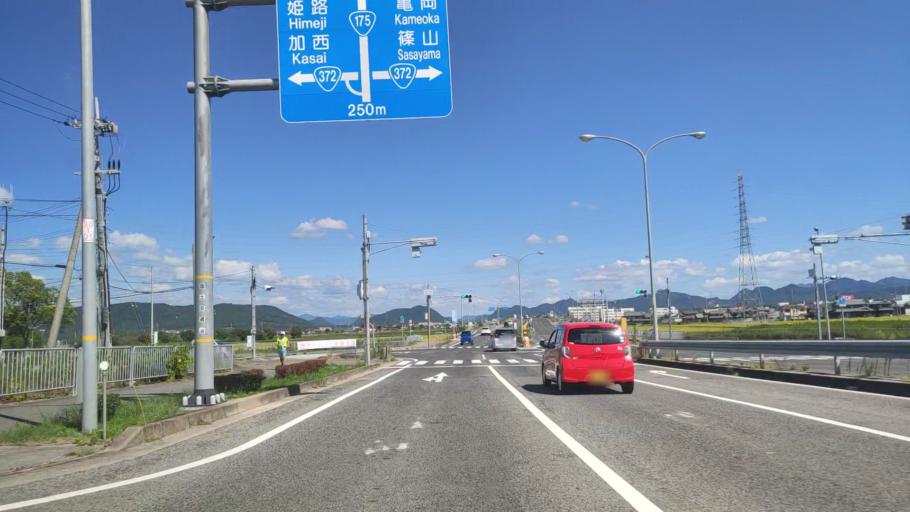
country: JP
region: Hyogo
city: Yashiro
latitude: 34.9075
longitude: 134.9530
